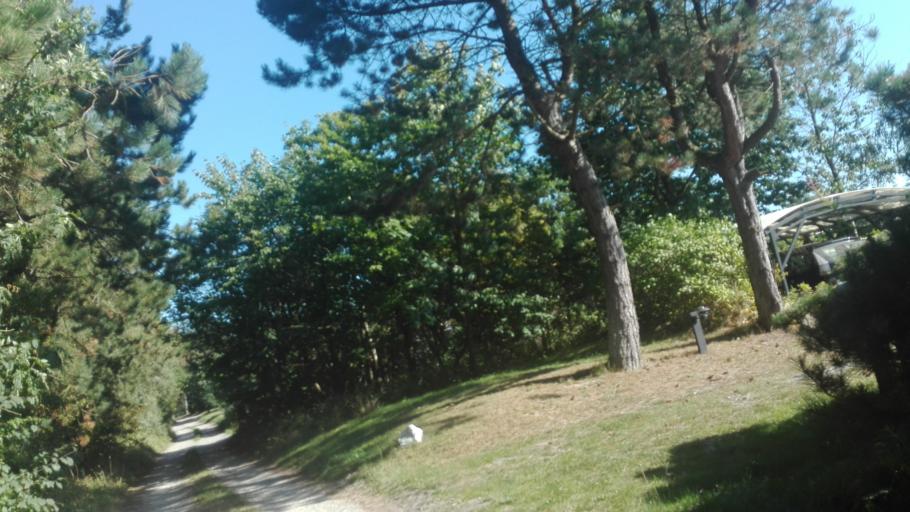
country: DK
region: Central Jutland
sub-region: Syddjurs Kommune
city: Ebeltoft
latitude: 56.2274
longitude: 10.7422
